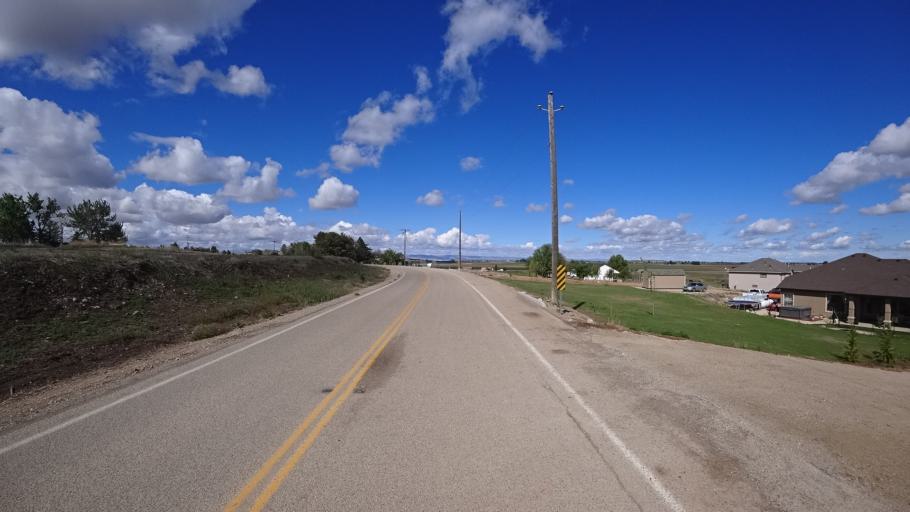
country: US
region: Idaho
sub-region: Ada County
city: Kuna
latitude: 43.4646
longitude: -116.4655
